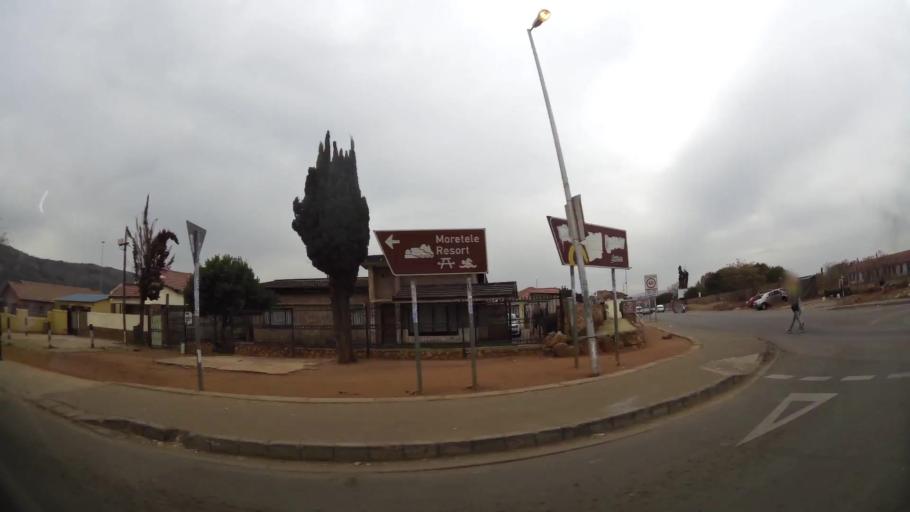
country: ZA
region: Gauteng
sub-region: City of Tshwane Metropolitan Municipality
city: Cullinan
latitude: -25.7093
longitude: 28.3617
